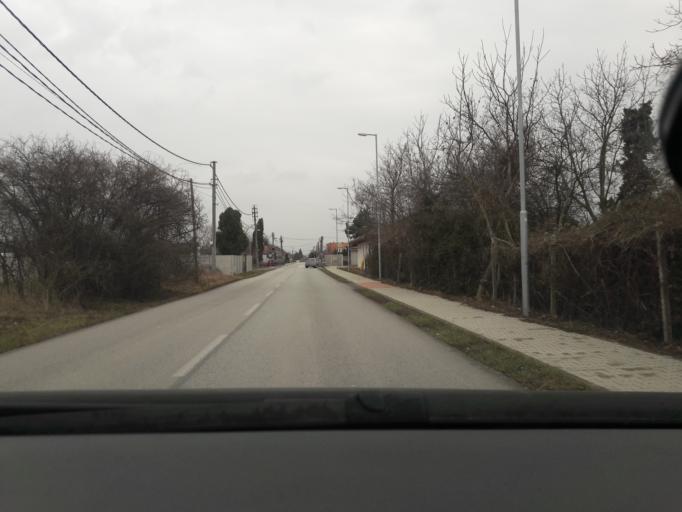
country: SK
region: Bratislavsky
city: Senec
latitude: 48.3160
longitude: 17.4392
